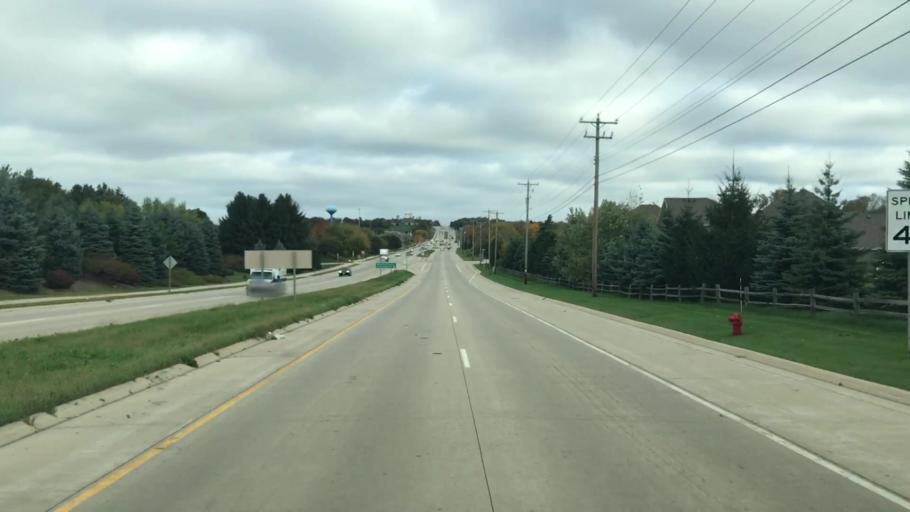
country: US
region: Wisconsin
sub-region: Waukesha County
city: Pewaukee
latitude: 43.0615
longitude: -88.2251
